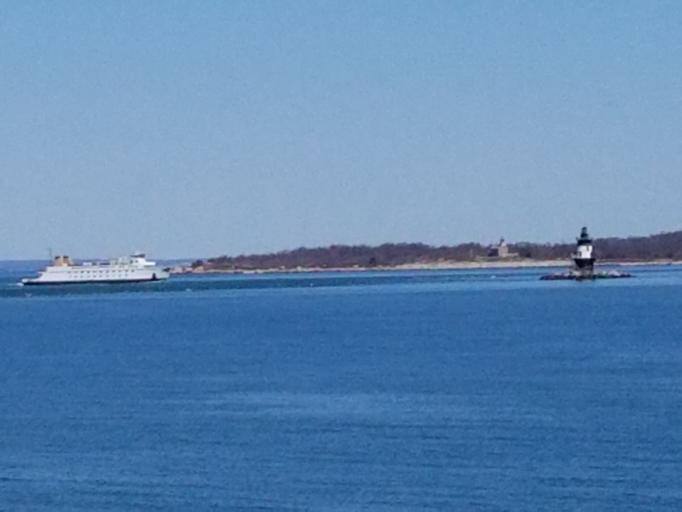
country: US
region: New York
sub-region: Suffolk County
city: Greenport
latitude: 41.1526
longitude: -72.2382
